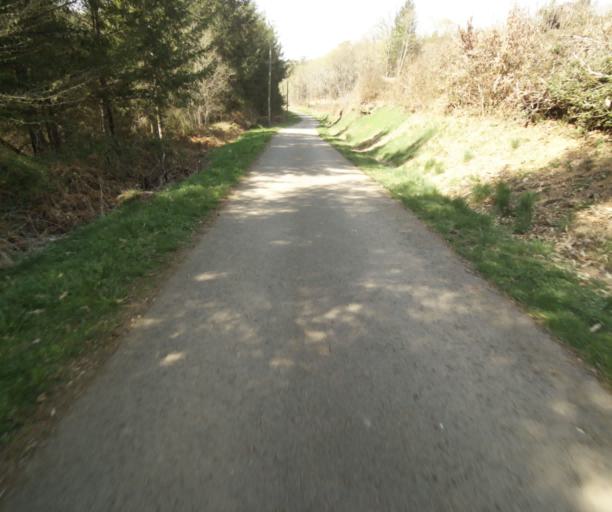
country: FR
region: Limousin
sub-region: Departement de la Correze
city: Seilhac
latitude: 45.3989
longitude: 1.7731
